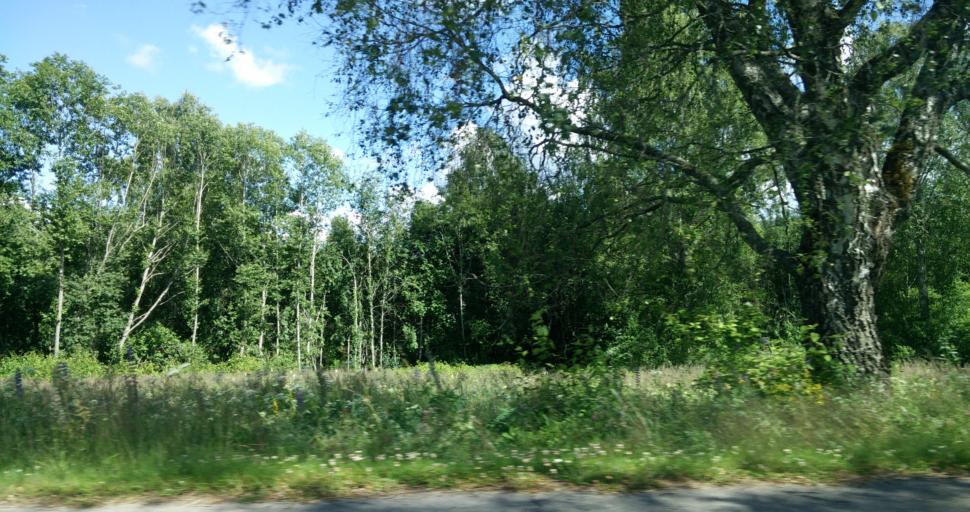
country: SE
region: Vaermland
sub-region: Hagfors Kommun
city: Hagfors
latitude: 60.0248
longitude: 13.6798
